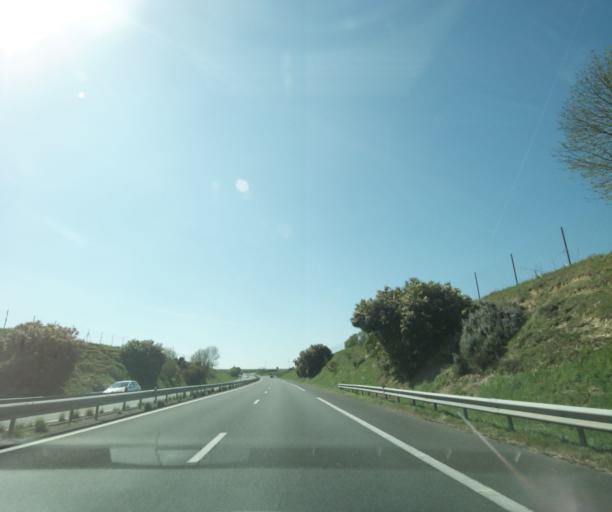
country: FR
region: Centre
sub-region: Departement de l'Indre
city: Vatan
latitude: 47.0673
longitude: 1.8206
